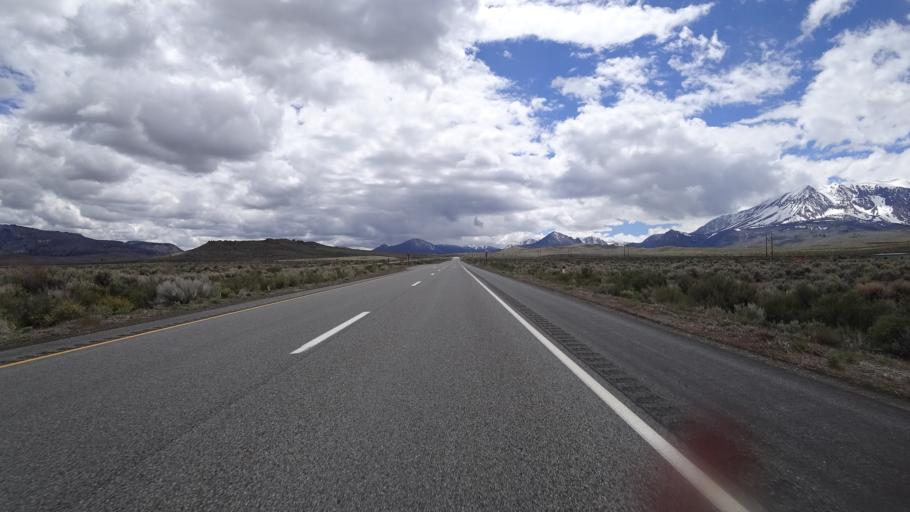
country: US
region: California
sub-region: Mono County
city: Mammoth Lakes
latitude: 37.8754
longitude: -119.0892
